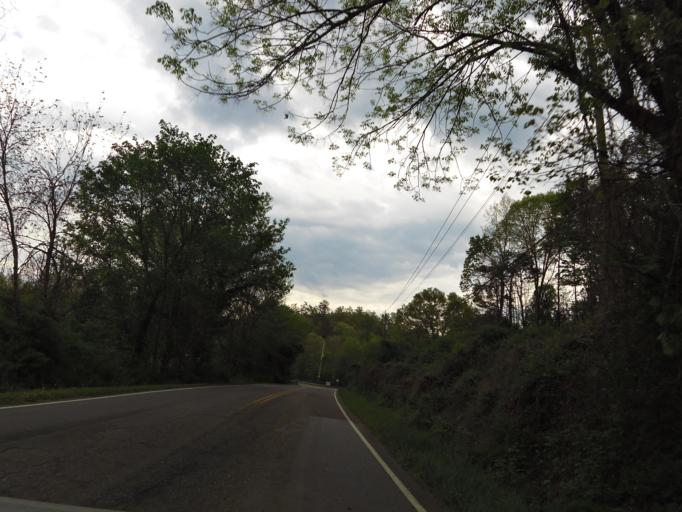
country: US
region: Tennessee
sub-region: Blount County
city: Wildwood
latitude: 35.8921
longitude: -83.8456
